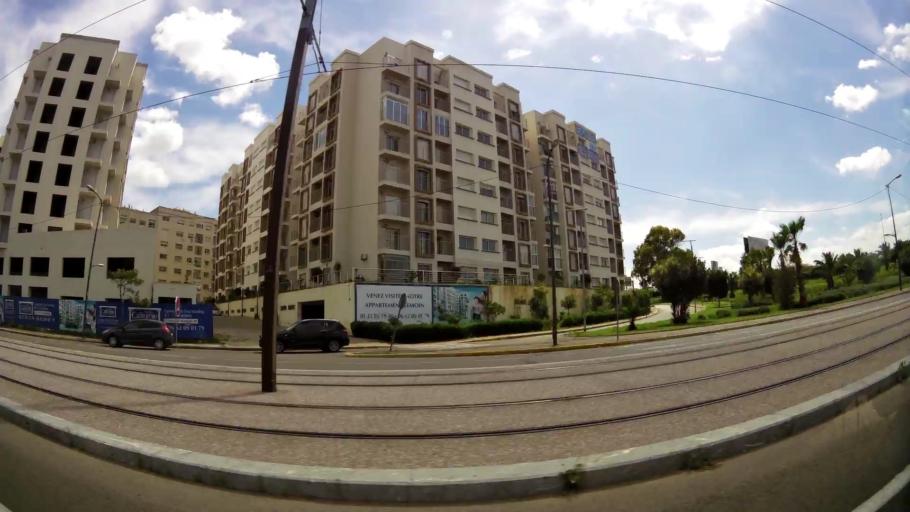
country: MA
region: Grand Casablanca
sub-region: Casablanca
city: Casablanca
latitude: 33.5532
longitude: -7.6318
